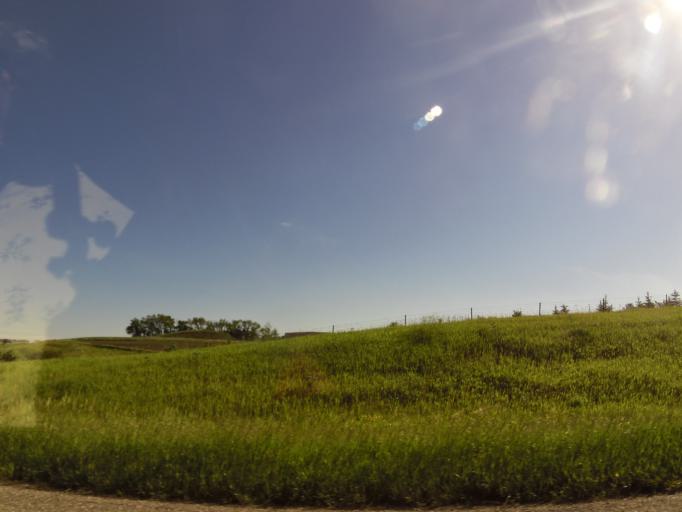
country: US
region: Minnesota
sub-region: Otter Tail County
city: Fergus Falls
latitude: 46.2609
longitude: -96.0885
